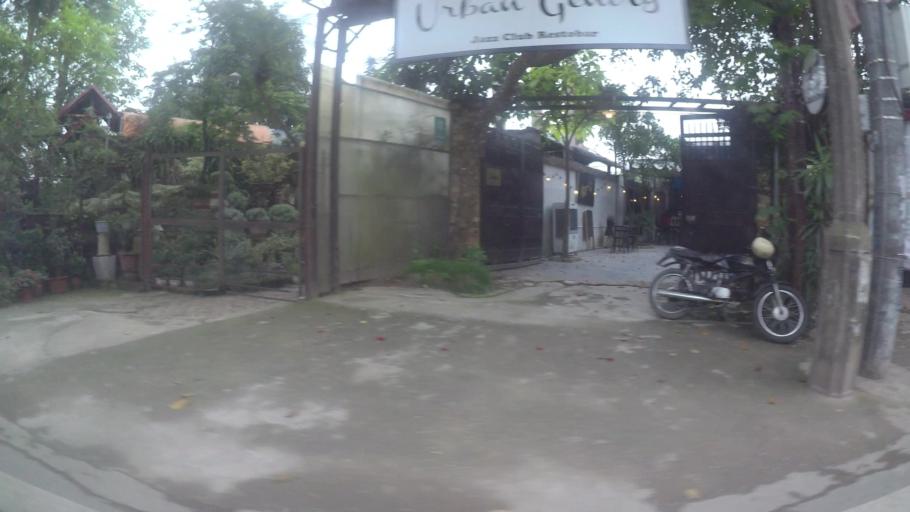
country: VN
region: Ha Noi
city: Tay Ho
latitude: 21.0617
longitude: 105.8240
